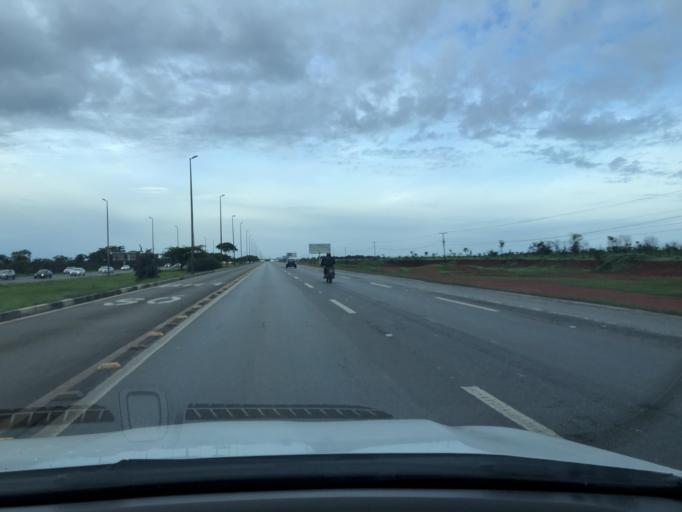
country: BR
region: Federal District
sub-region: Brasilia
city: Brasilia
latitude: -15.9608
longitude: -47.9932
